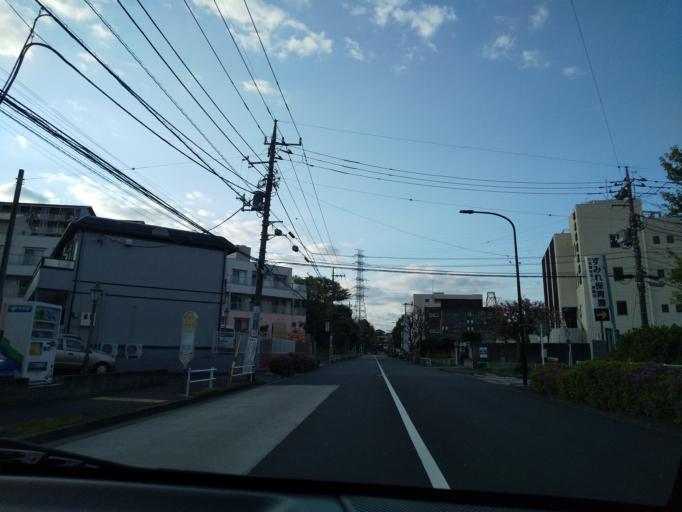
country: JP
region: Tokyo
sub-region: Machida-shi
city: Machida
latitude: 35.5570
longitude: 139.4260
